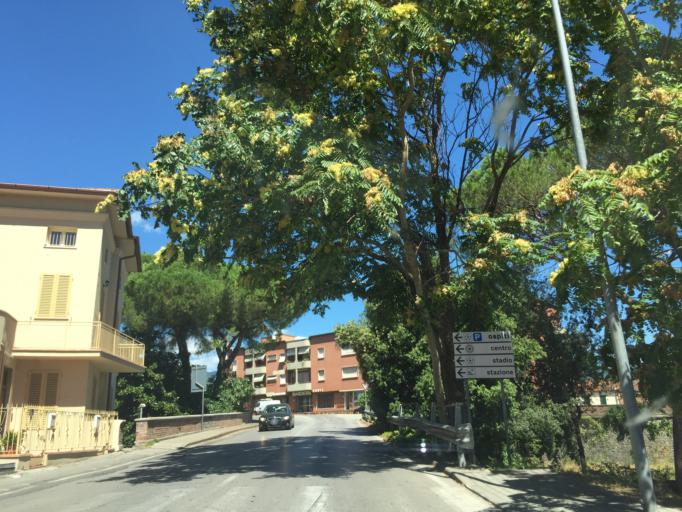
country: IT
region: Tuscany
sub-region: Provincia di Pistoia
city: Pistoia
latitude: 43.9260
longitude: 10.9192
